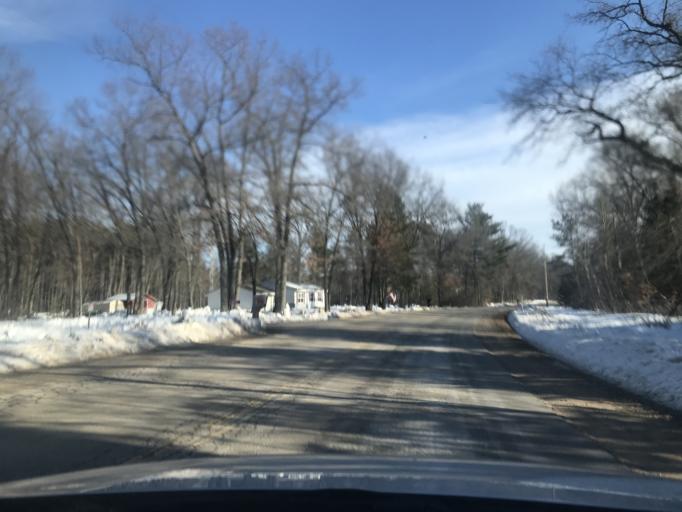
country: US
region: Wisconsin
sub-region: Marinette County
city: Peshtigo
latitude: 45.0310
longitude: -87.7117
